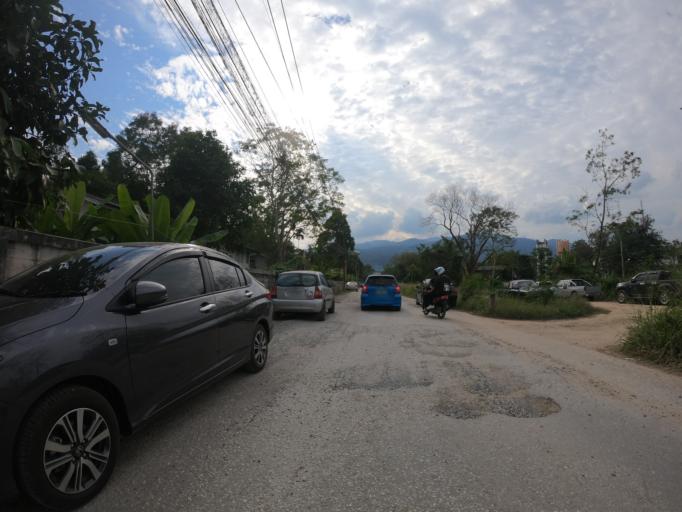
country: TH
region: Chiang Mai
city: Chiang Mai
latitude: 18.8526
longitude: 98.9650
